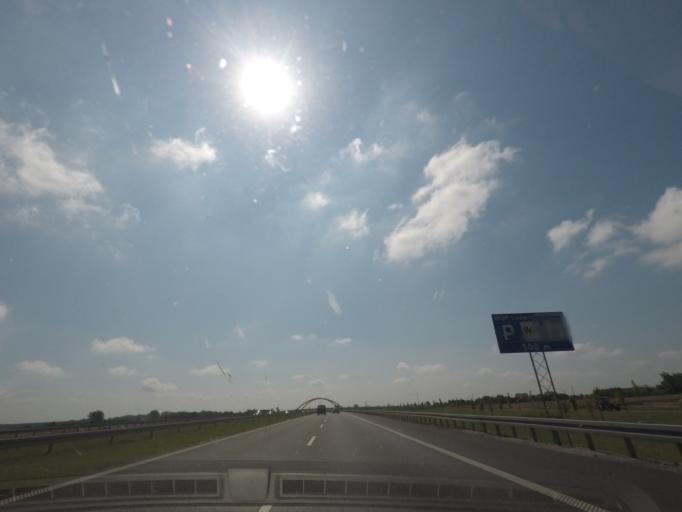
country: PL
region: Kujawsko-Pomorskie
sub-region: Powiat wloclawski
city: Chocen
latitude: 52.5746
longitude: 19.0043
